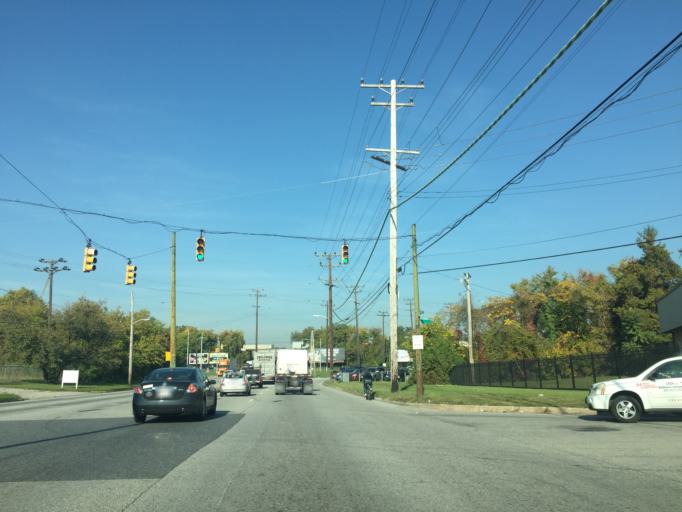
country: US
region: Maryland
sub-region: Baltimore County
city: Rosedale
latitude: 39.3004
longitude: -76.5358
